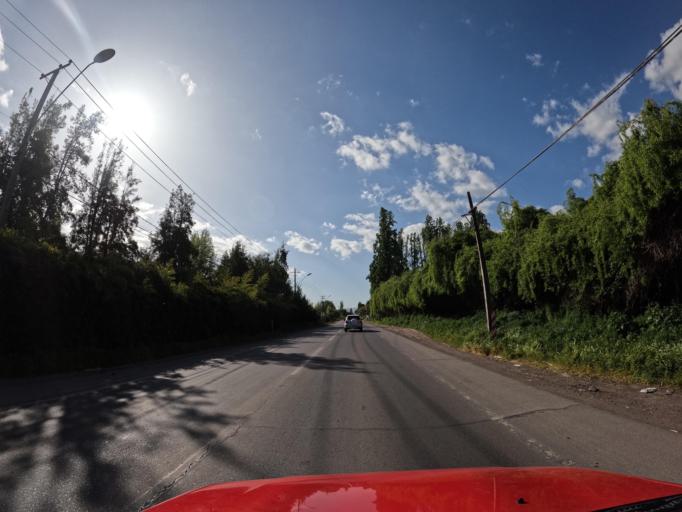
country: CL
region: Maule
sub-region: Provincia de Curico
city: Curico
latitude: -34.9533
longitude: -71.2553
